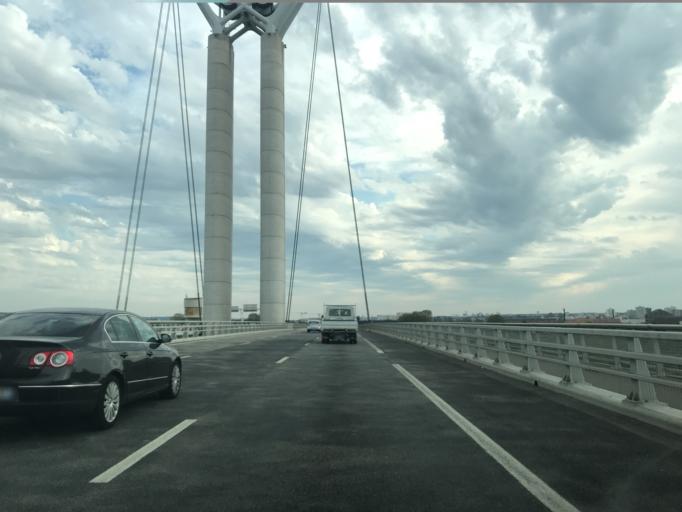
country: FR
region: Haute-Normandie
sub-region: Departement de la Seine-Maritime
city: Deville-les-Rouen
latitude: 49.4441
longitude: 1.0639
